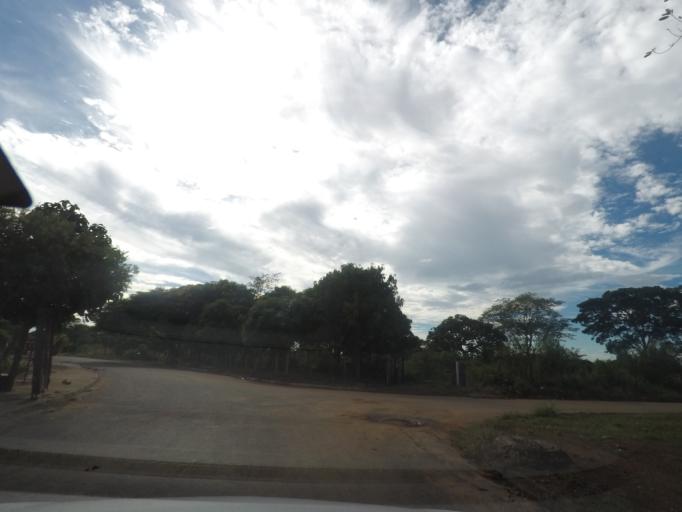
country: BR
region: Goias
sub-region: Aparecida De Goiania
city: Aparecida de Goiania
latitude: -16.8349
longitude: -49.2941
